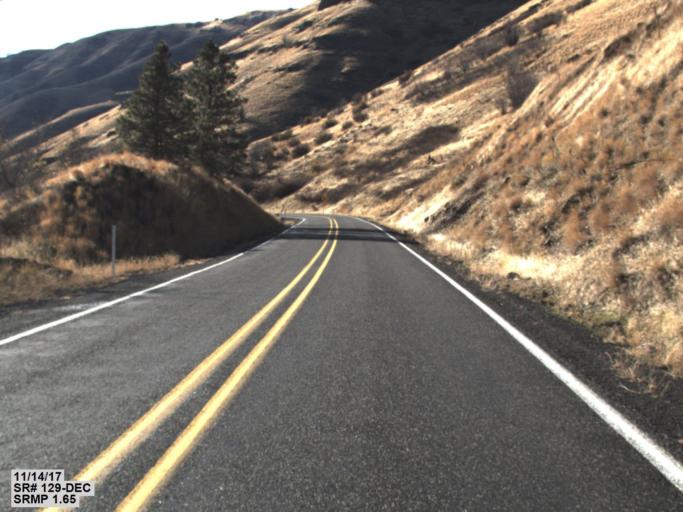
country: US
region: Washington
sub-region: Asotin County
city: Asotin
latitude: 46.0086
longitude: -117.2774
